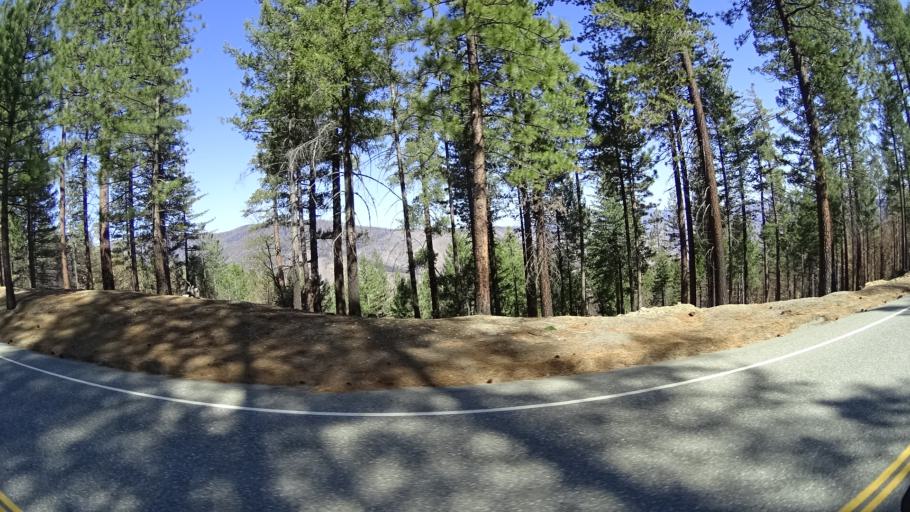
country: US
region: California
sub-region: Tehama County
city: Rancho Tehama Reserve
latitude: 39.6516
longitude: -122.7351
